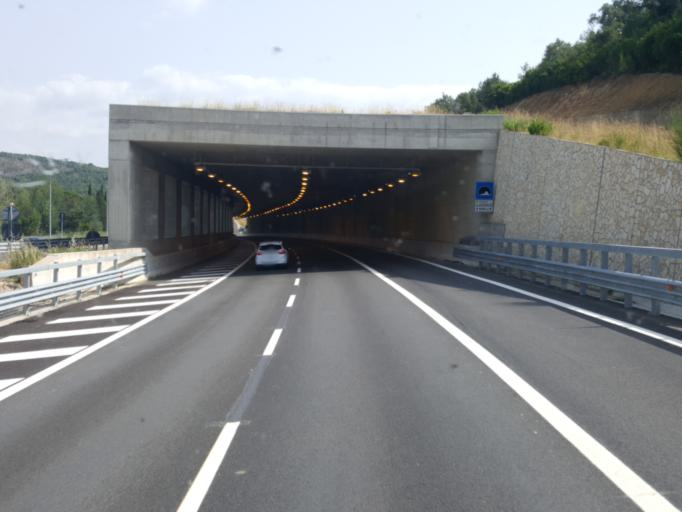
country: IT
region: Tuscany
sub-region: Provincia di Grosseto
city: Civitella Marittima
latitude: 43.0513
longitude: 11.2838
